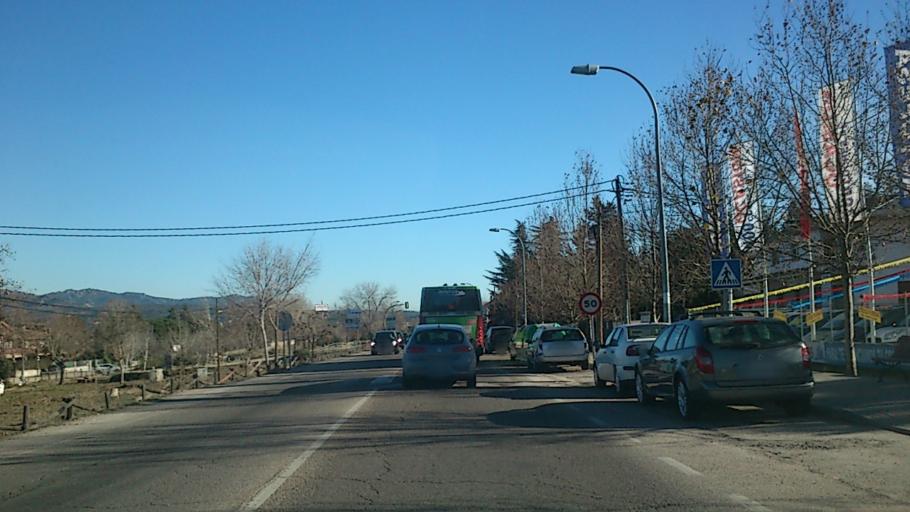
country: ES
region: Madrid
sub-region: Provincia de Madrid
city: Alpedrete
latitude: 40.6403
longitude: -4.0296
